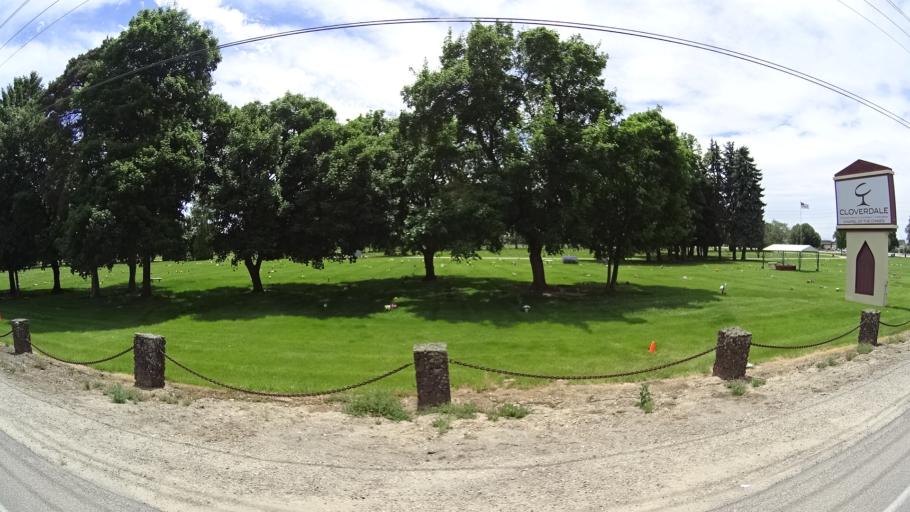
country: US
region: Idaho
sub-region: Ada County
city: Meridian
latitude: 43.6194
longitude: -116.3324
